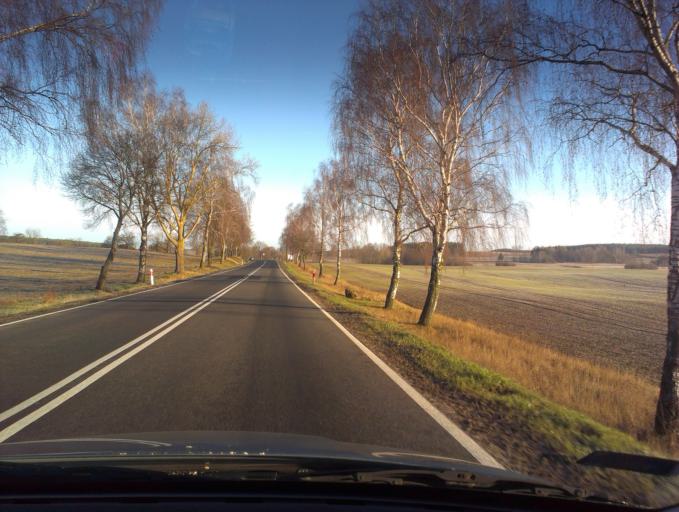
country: PL
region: West Pomeranian Voivodeship
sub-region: Powiat szczecinecki
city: Szczecinek
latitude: 53.7551
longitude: 16.6521
